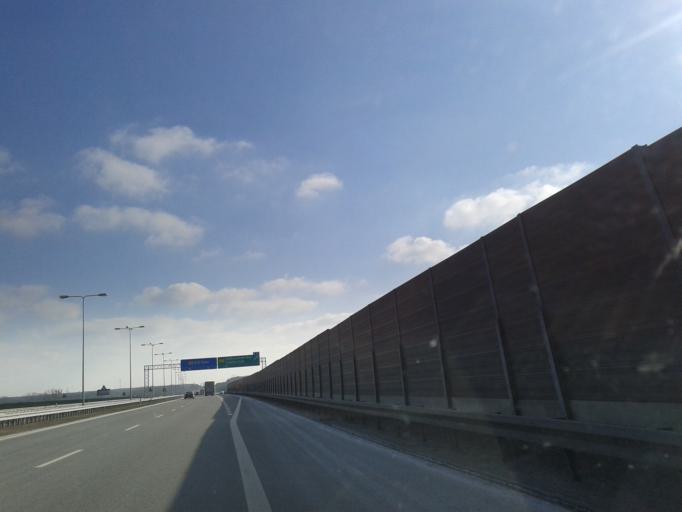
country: PL
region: Kujawsko-Pomorskie
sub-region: Powiat aleksandrowski
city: Ciechocinek
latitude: 52.8697
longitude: 18.7552
